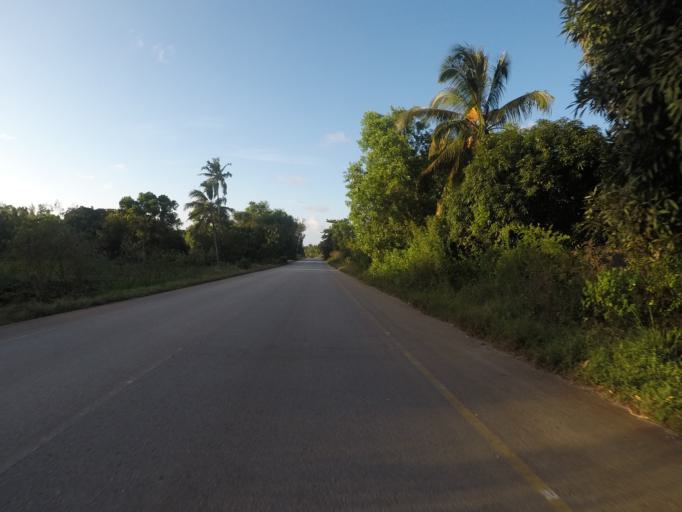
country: TZ
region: Zanzibar North
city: Kijini
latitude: -5.8488
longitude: 39.2836
